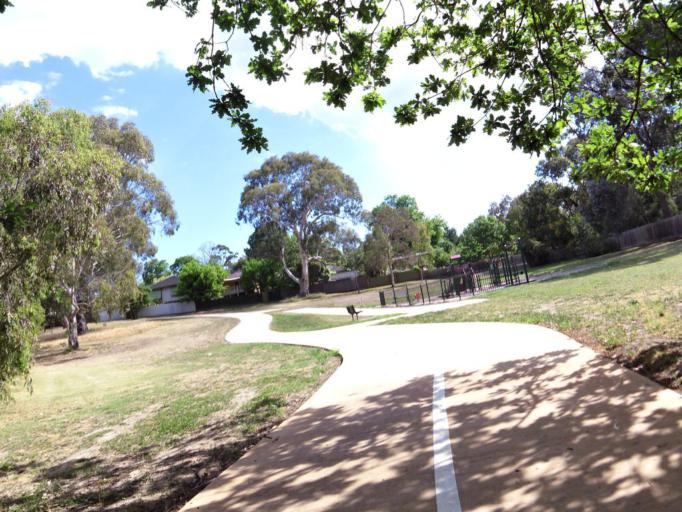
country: AU
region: Victoria
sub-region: Banyule
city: Viewbank
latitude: -37.7443
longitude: 145.0803
